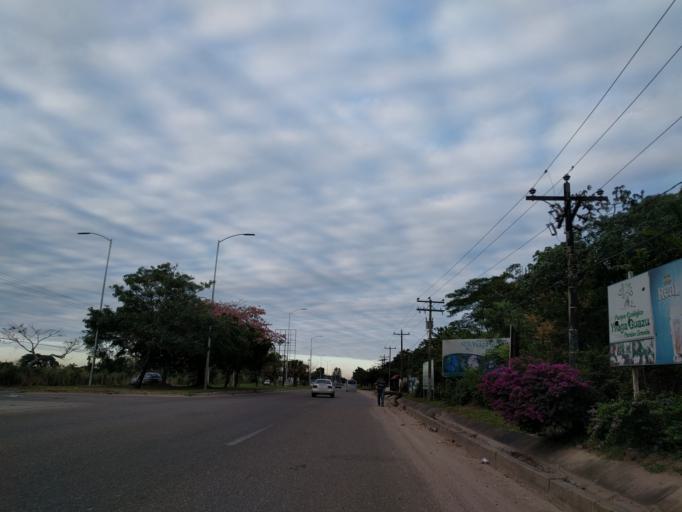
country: BO
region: Santa Cruz
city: Santa Cruz de la Sierra
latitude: -17.8670
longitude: -63.2704
